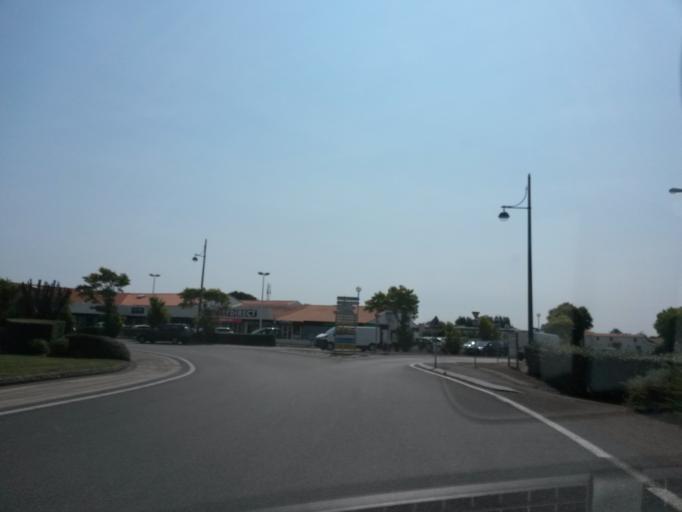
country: FR
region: Pays de la Loire
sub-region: Departement de la Vendee
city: La Tranche-sur-Mer
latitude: 46.3520
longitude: -1.4295
